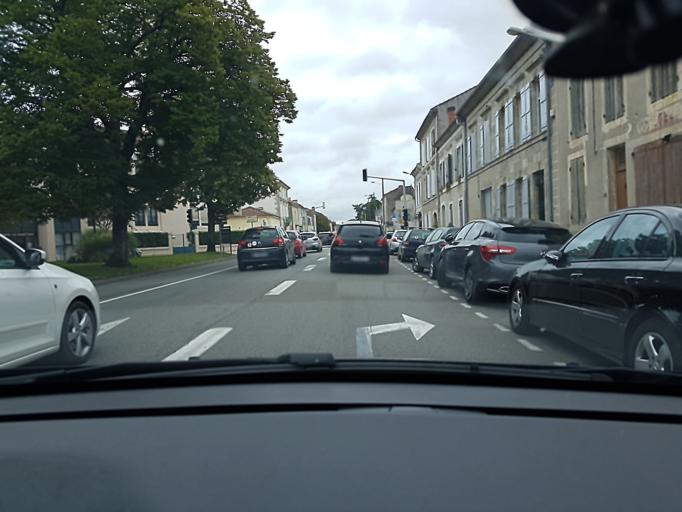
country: FR
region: Aquitaine
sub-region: Departement du Lot-et-Garonne
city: Nerac
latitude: 44.1344
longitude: 0.3443
